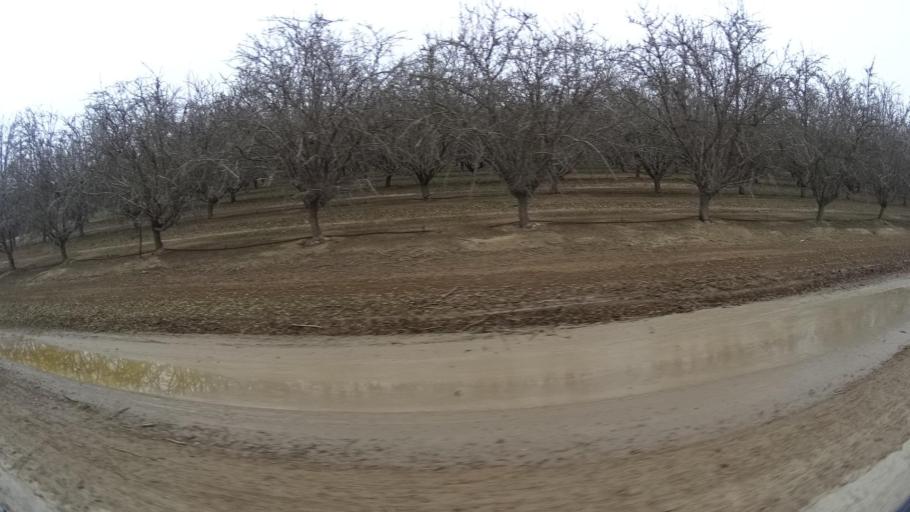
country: US
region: California
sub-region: Kern County
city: Wasco
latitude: 35.5789
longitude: -119.5094
